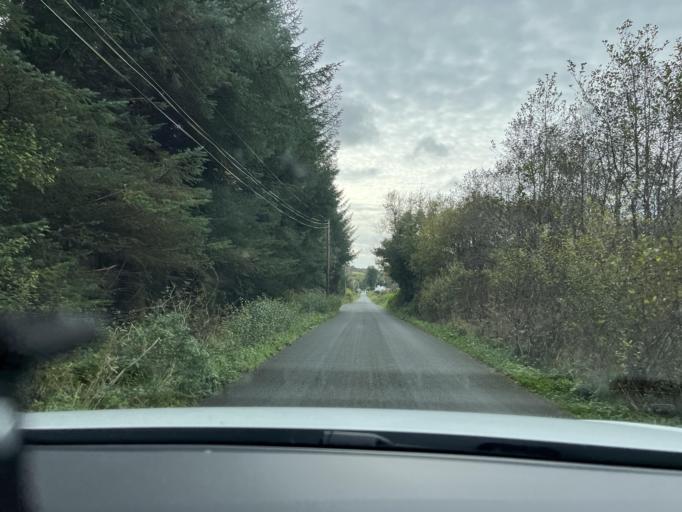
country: IE
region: Connaught
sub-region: Roscommon
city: Boyle
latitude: 54.0243
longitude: -8.3406
